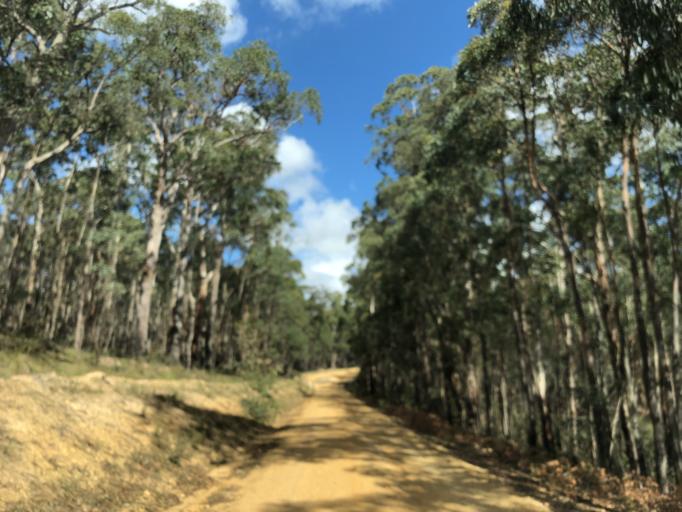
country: AU
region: Victoria
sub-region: Moorabool
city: Bacchus Marsh
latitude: -37.5207
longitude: 144.3215
